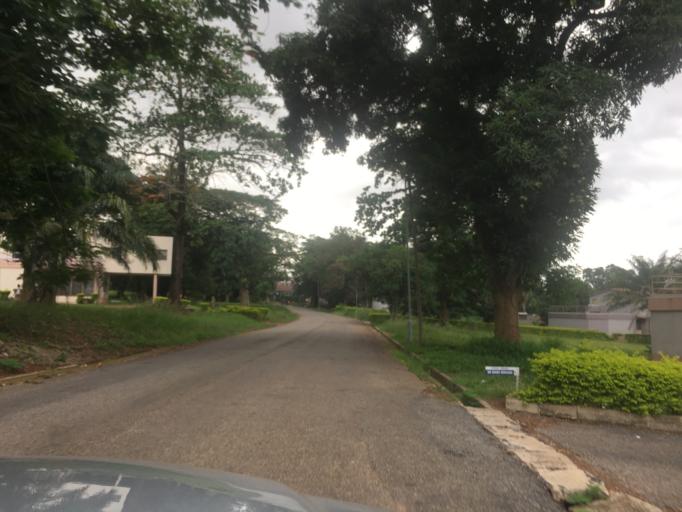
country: GH
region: Ashanti
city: Kumasi
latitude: 6.6798
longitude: -1.5809
